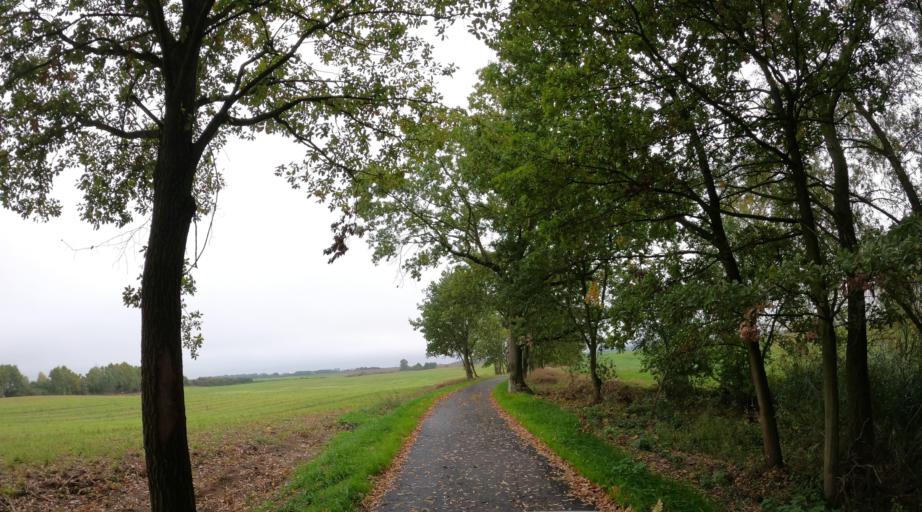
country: PL
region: West Pomeranian Voivodeship
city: Trzcinsko Zdroj
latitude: 52.9304
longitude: 14.7268
